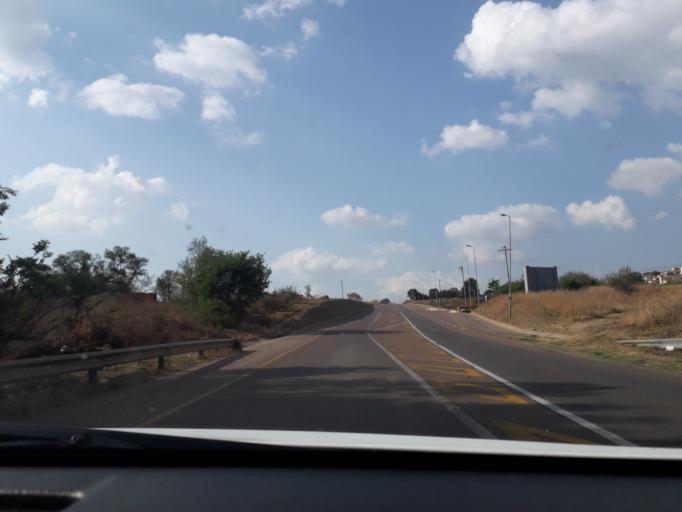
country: ZA
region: Gauteng
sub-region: City of Tshwane Metropolitan Municipality
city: Centurion
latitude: -25.8782
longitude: 28.2562
